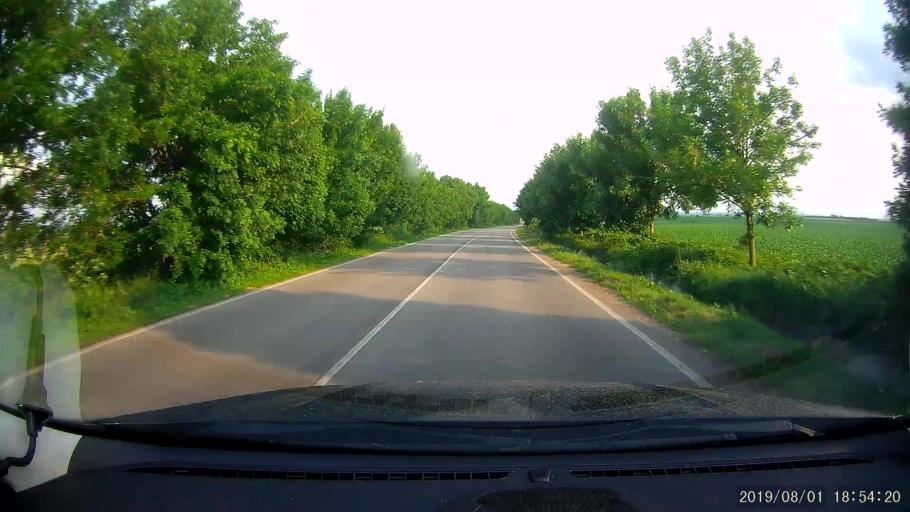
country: BG
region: Shumen
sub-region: Obshtina Shumen
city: Shumen
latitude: 43.2010
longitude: 27.0013
